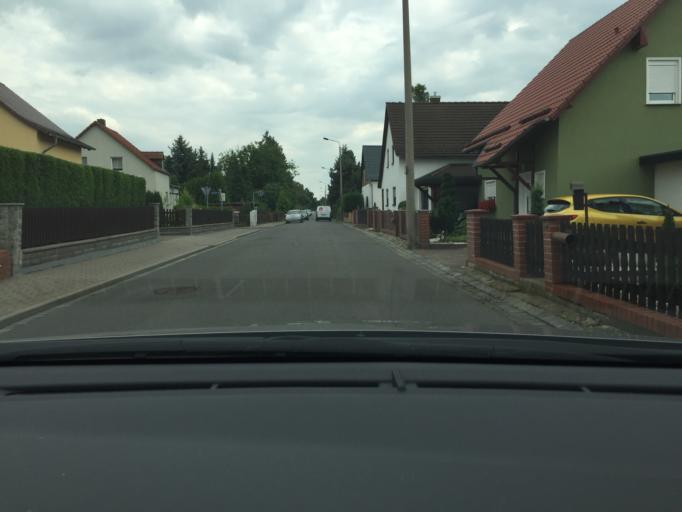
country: DE
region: Saxony
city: Taucha
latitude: 51.3854
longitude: 12.4628
